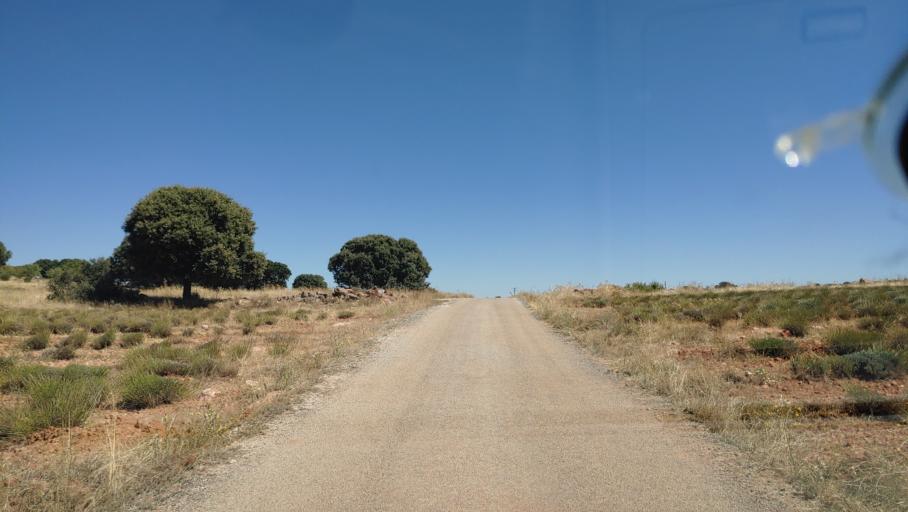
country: ES
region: Castille-La Mancha
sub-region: Provincia de Albacete
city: Ossa de Montiel
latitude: 38.9333
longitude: -2.7658
